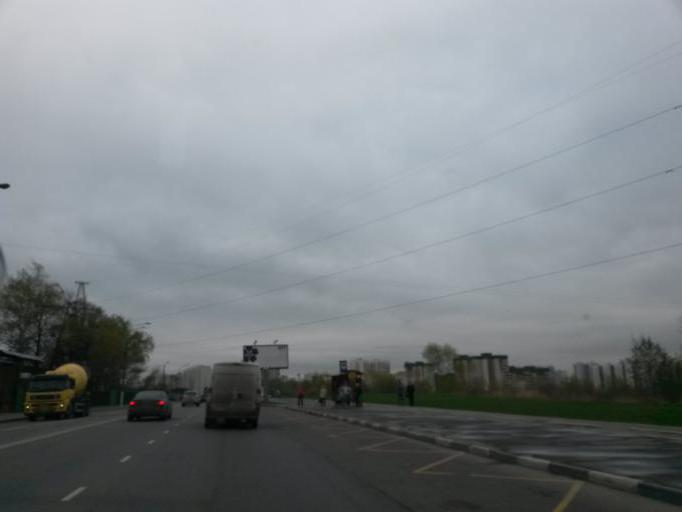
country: RU
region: Moscow
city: Mar'ino
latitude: 55.6353
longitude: 37.7274
